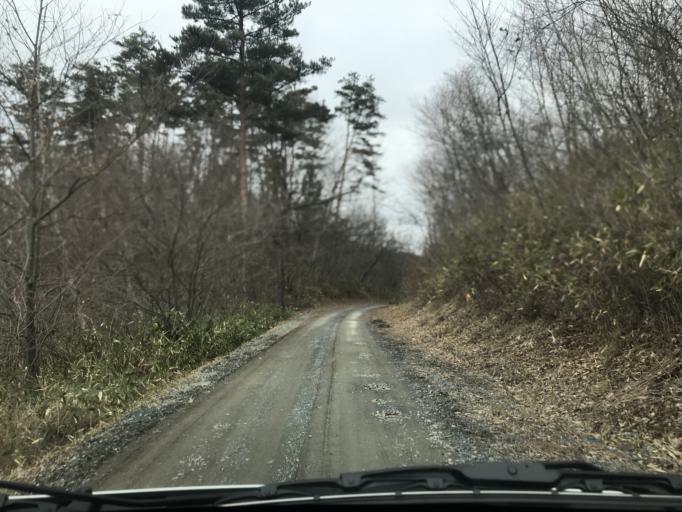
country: JP
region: Iwate
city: Kitakami
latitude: 39.3202
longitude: 141.2276
